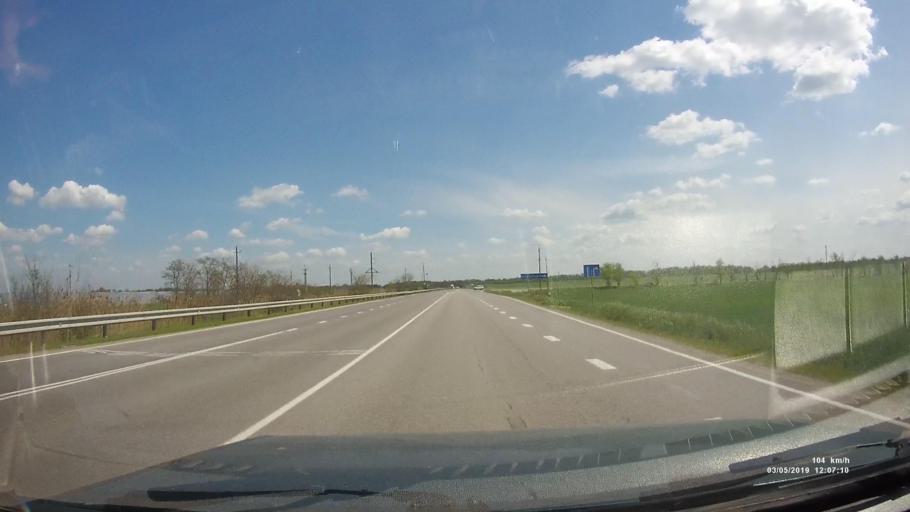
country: RU
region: Rostov
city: Bagayevskaya
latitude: 47.2849
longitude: 40.4686
